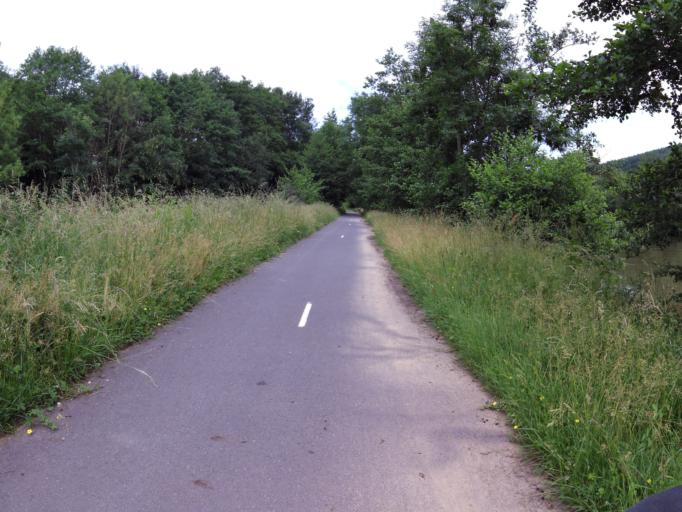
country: FR
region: Champagne-Ardenne
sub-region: Departement des Ardennes
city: Nouzonville
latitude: 49.8216
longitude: 4.7435
